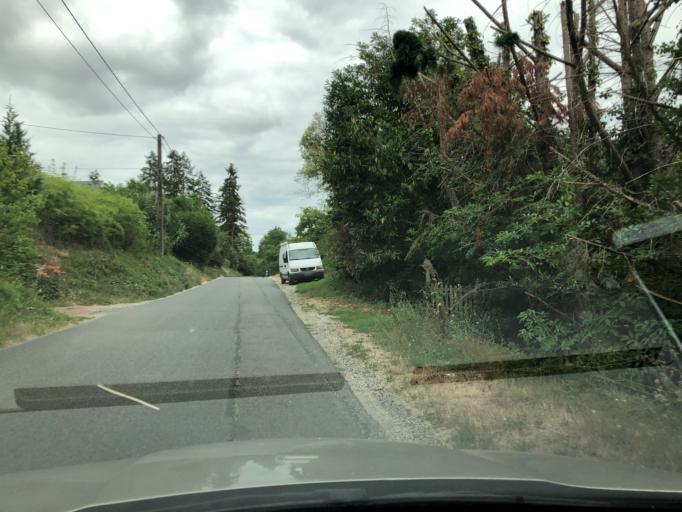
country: FR
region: Centre
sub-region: Departement d'Indre-et-Loire
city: Saint-Etienne-de-Chigny
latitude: 47.3724
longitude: 0.5229
